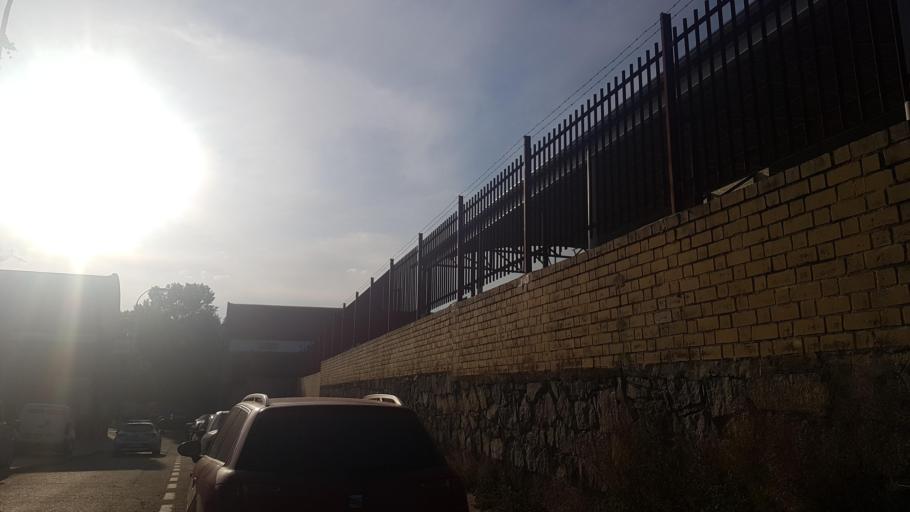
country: ES
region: Madrid
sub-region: Provincia de Madrid
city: Puente de Vallecas
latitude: 40.3701
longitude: -3.6578
